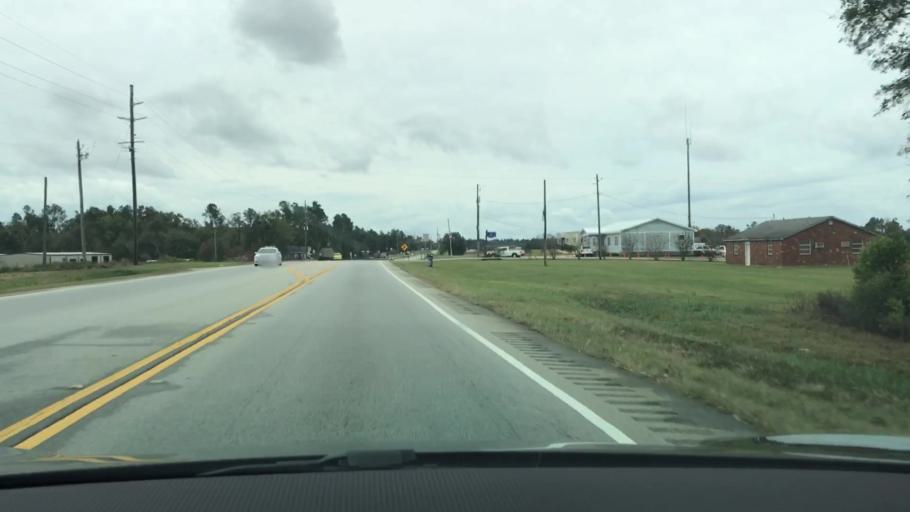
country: US
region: Georgia
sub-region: Jefferson County
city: Louisville
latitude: 33.0317
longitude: -82.4052
